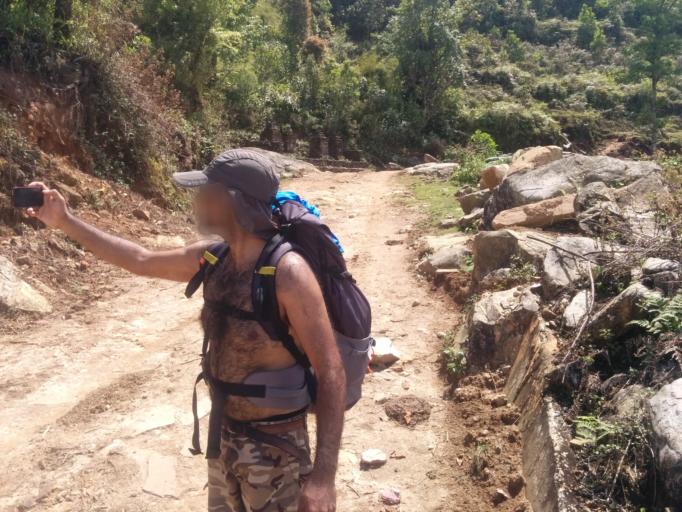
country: NP
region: Western Region
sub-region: Gandaki Zone
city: Pokhara
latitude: 28.2273
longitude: 83.8480
